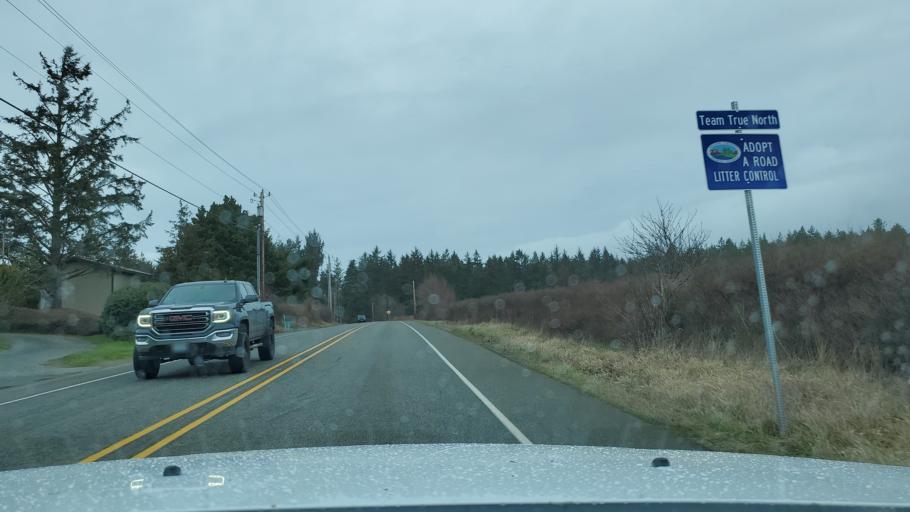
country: US
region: Washington
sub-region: Island County
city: Ault Field
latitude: 48.2846
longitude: -122.7273
